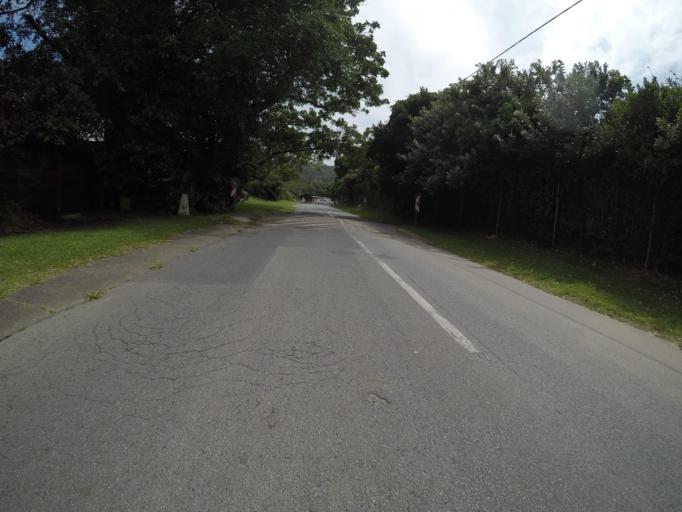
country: ZA
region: Eastern Cape
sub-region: Buffalo City Metropolitan Municipality
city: East London
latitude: -32.9348
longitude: 28.0294
